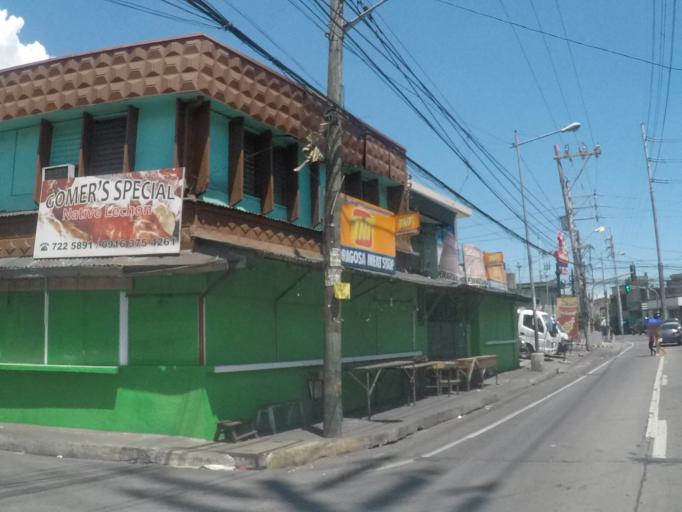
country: PH
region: Metro Manila
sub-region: San Juan
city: San Juan
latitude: 14.5961
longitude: 121.0277
